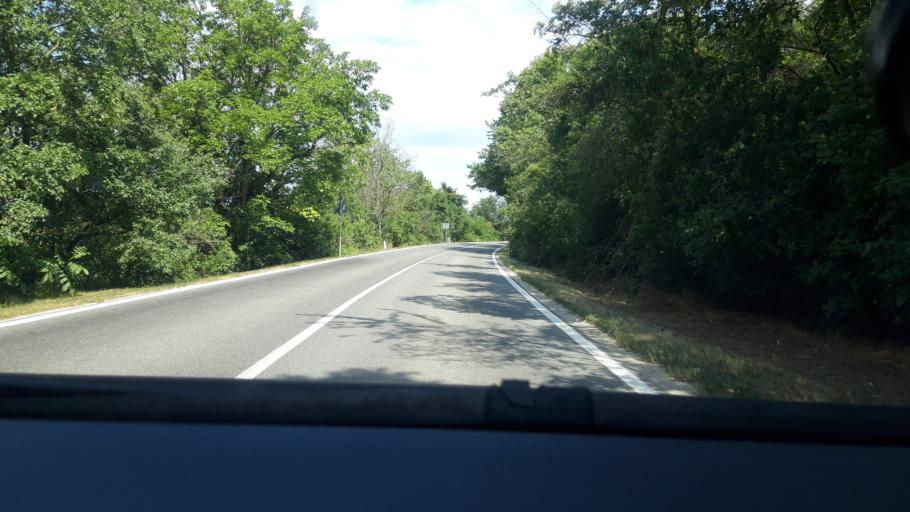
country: SK
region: Trnavsky
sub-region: Okres Trnava
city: Piestany
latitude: 48.6377
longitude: 17.8637
